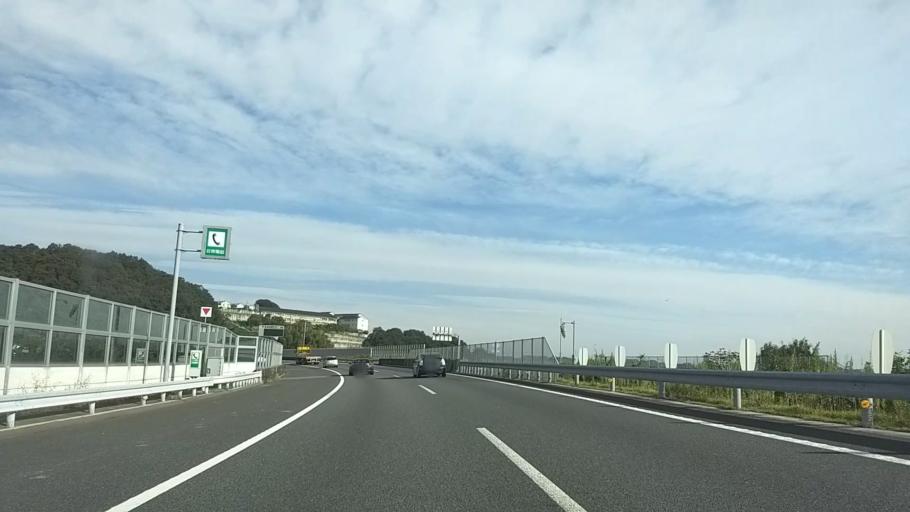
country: JP
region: Kanagawa
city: Zama
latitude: 35.5064
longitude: 139.3661
